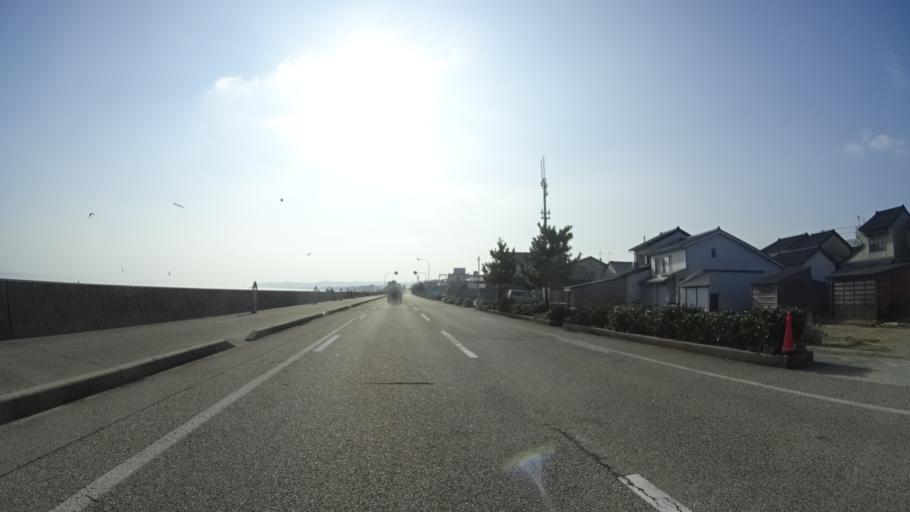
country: JP
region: Toyama
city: Himi
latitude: 36.8511
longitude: 136.9928
